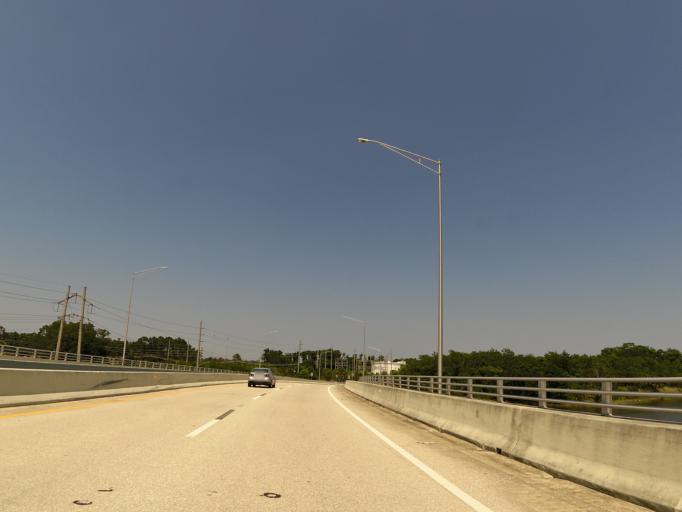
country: US
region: Florida
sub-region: Duval County
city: Jacksonville
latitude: 30.4171
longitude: -81.6022
